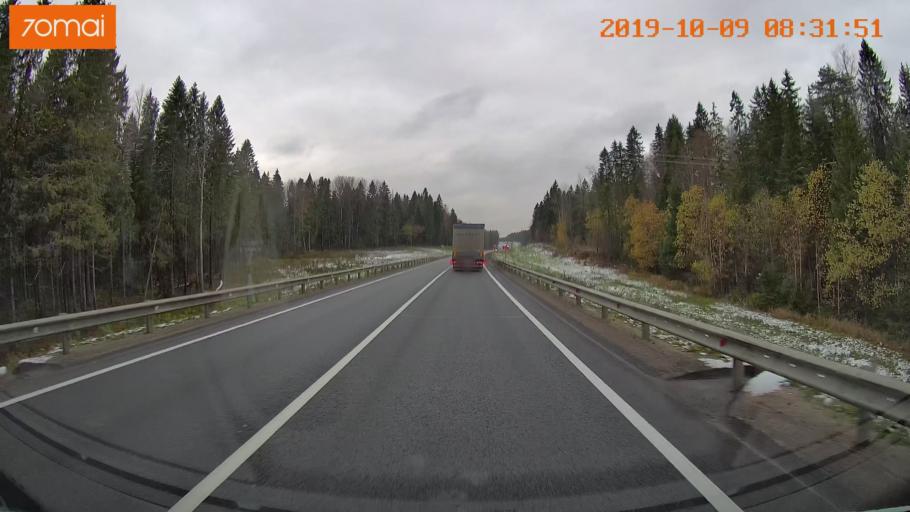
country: RU
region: Vologda
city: Gryazovets
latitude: 58.8591
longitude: 40.1994
